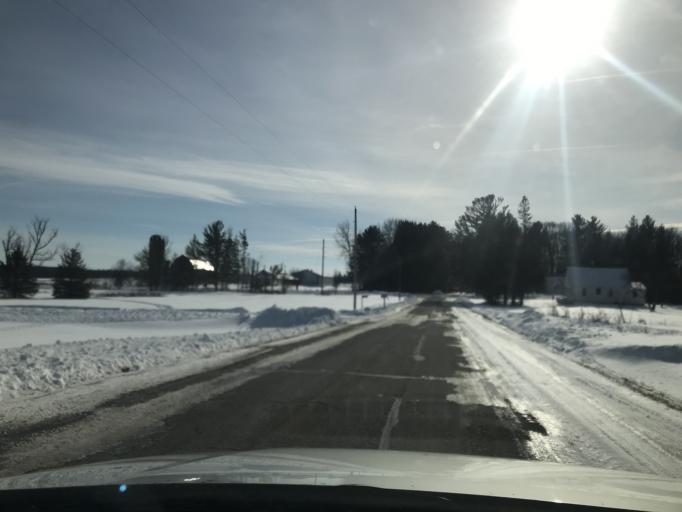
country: US
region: Wisconsin
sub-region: Oconto County
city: Gillett
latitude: 45.1141
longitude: -88.2402
